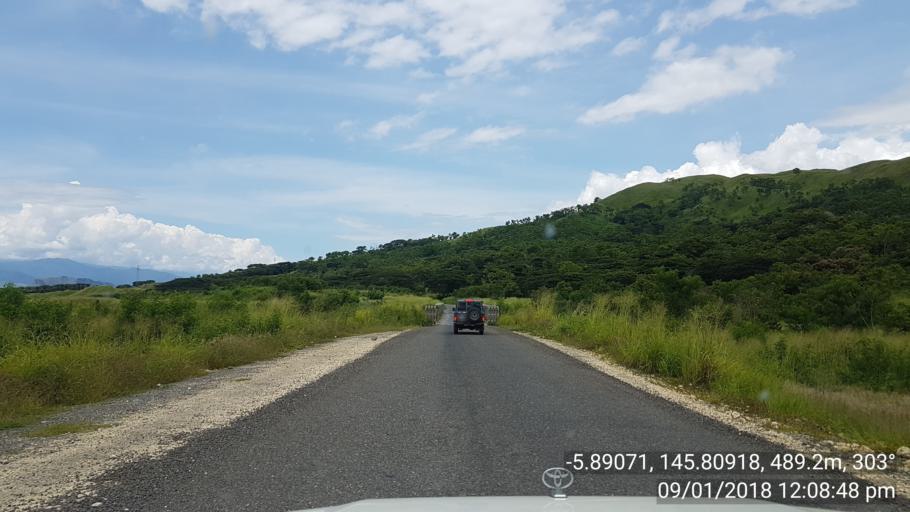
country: PG
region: Eastern Highlands
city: Kainantu
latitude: -5.8907
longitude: 145.8095
